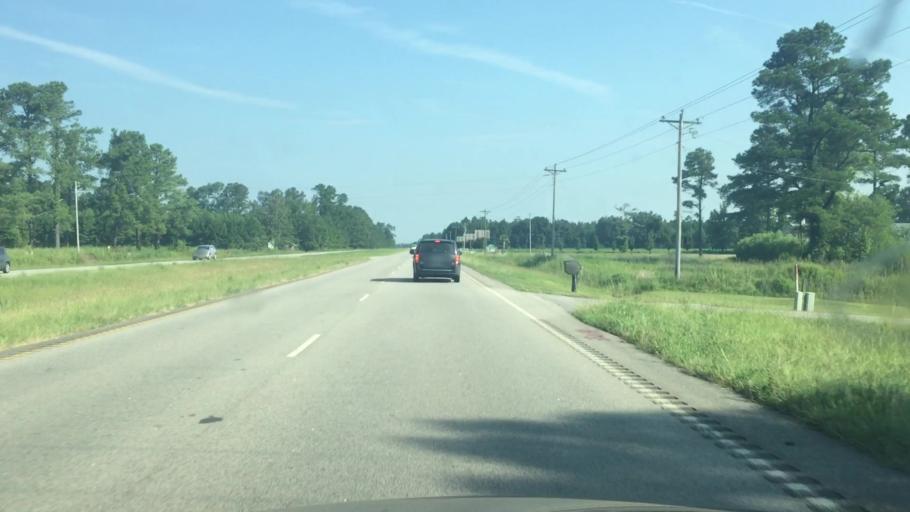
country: US
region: South Carolina
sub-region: Horry County
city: Little River
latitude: 33.9673
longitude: -78.7397
